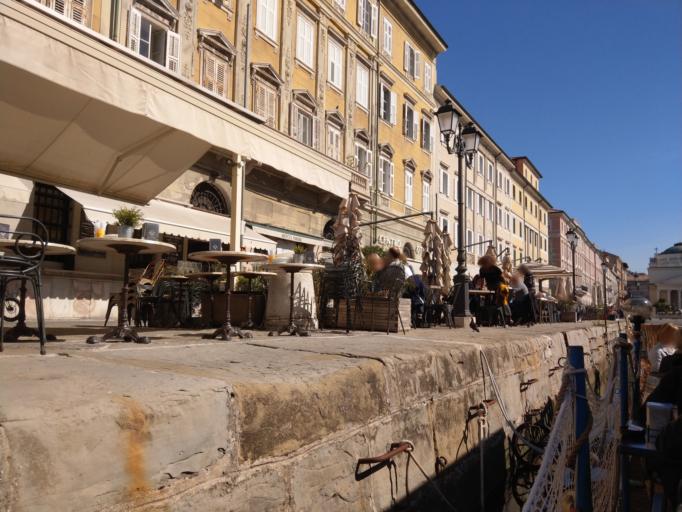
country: IT
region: Friuli Venezia Giulia
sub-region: Provincia di Trieste
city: Trieste
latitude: 45.6526
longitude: 13.7713
